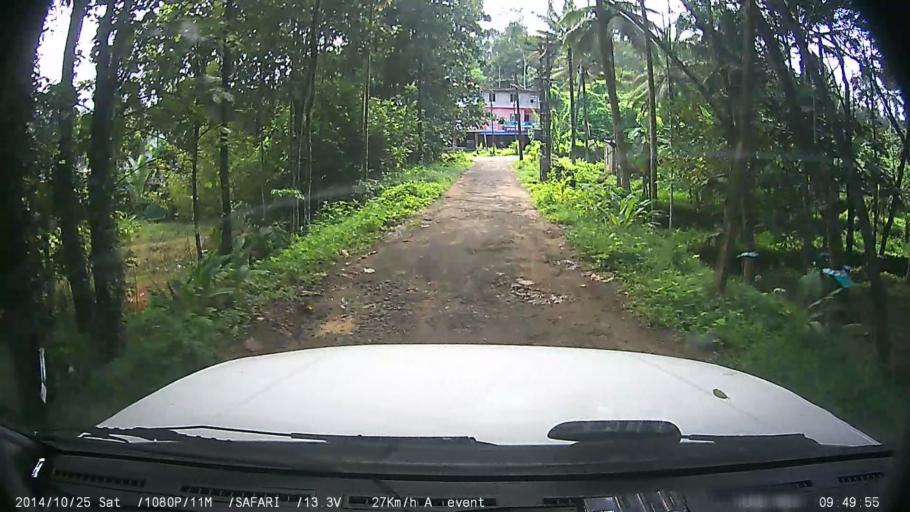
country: IN
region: Kerala
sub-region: Kottayam
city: Palackattumala
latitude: 9.7839
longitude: 76.5768
